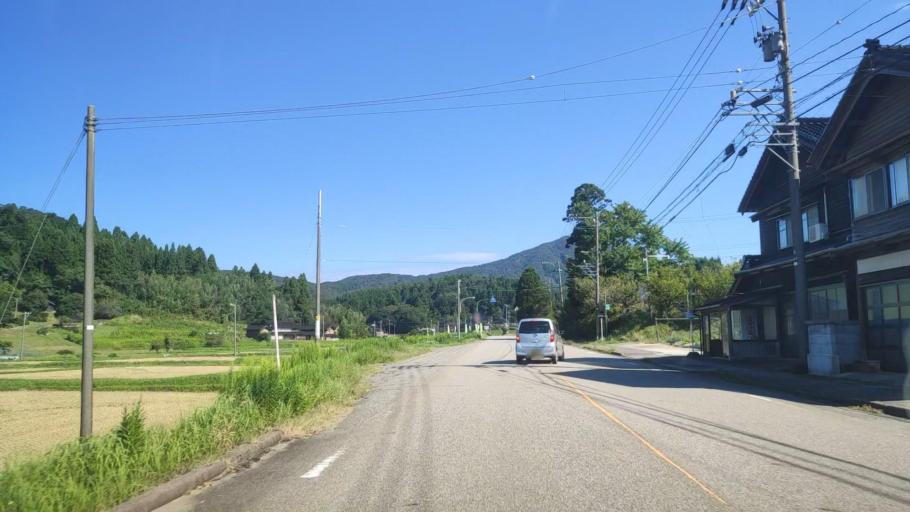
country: JP
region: Ishikawa
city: Nanao
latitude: 37.1890
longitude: 136.7163
